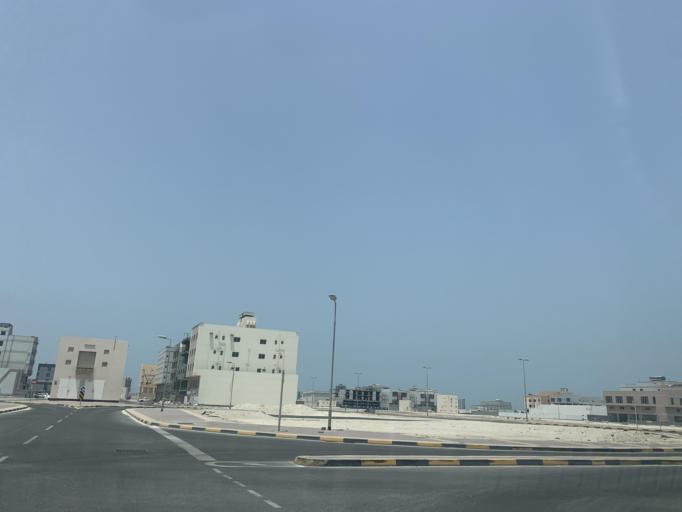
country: BH
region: Muharraq
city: Al Hadd
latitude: 26.2566
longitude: 50.6654
